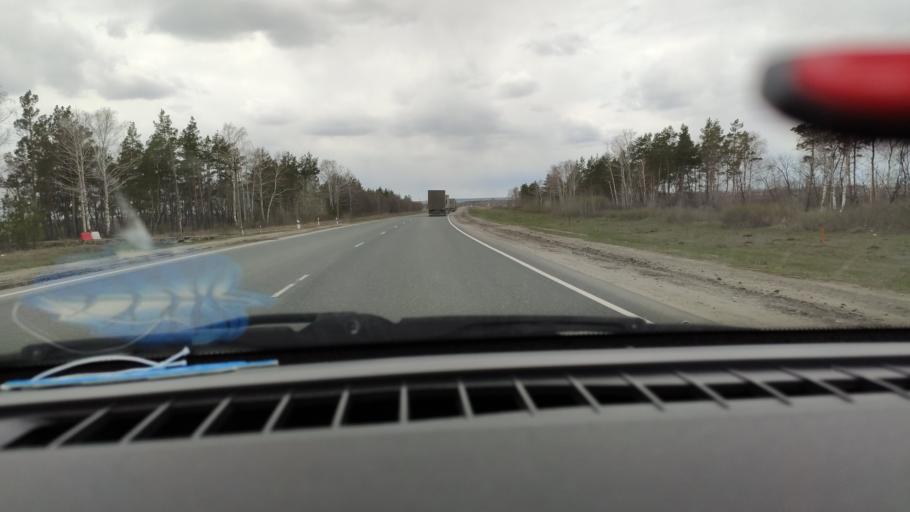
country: RU
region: Saratov
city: Sennoy
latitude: 52.1509
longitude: 46.9894
